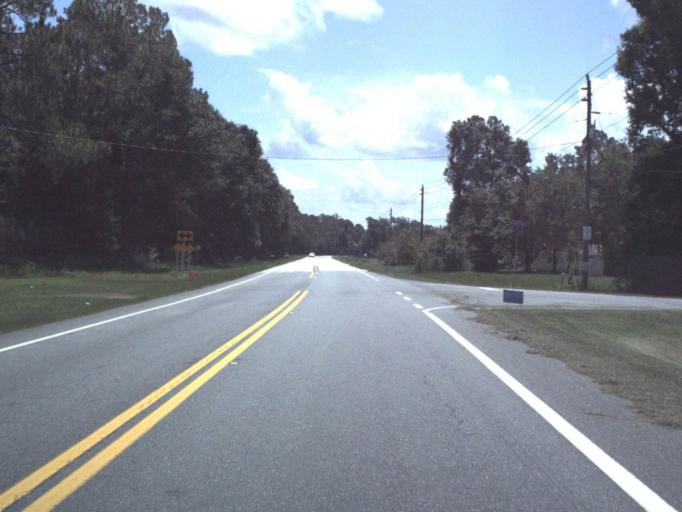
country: US
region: Florida
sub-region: Bradford County
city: Starke
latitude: 30.0195
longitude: -82.1507
